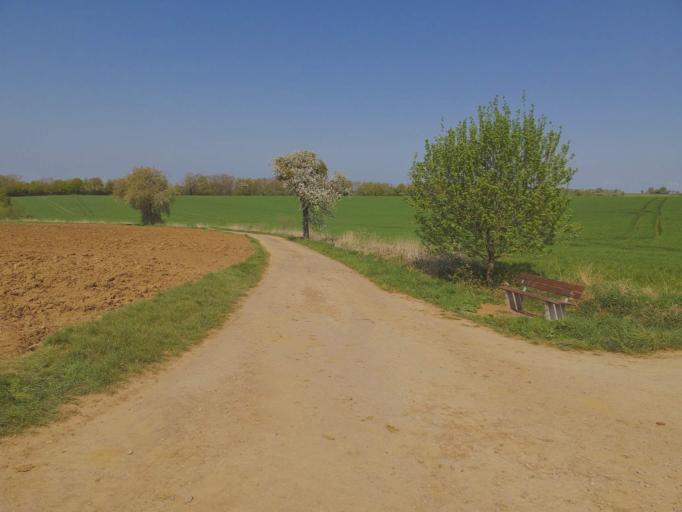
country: DE
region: Rheinland-Pfalz
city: Kirf
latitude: 49.5500
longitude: 6.4427
